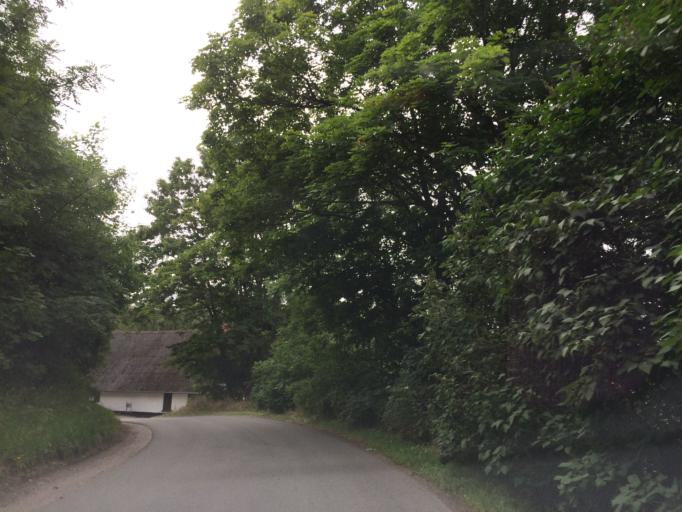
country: DK
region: Central Jutland
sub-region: Syddjurs Kommune
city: Ebeltoft
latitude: 56.2690
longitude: 10.7404
